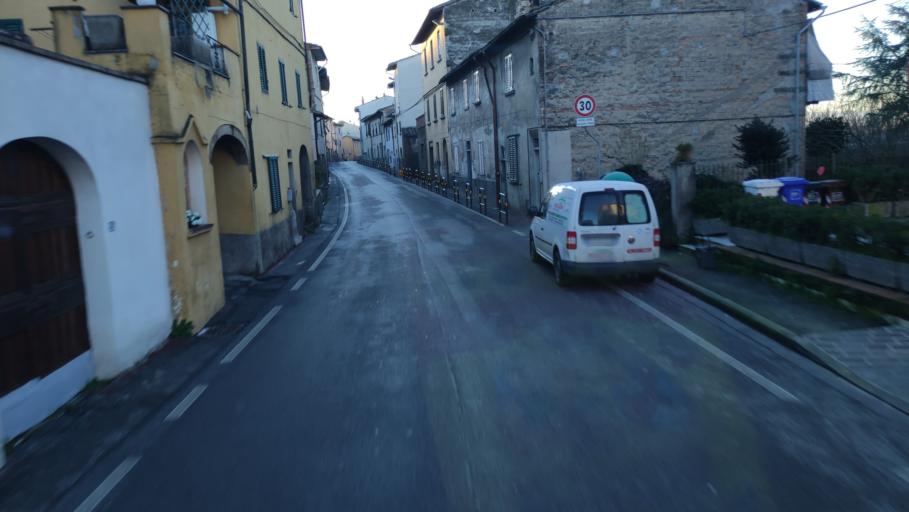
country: IT
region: Tuscany
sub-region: Province of Florence
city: Pozzale-Case Nuove
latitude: 43.6562
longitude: 10.9410
